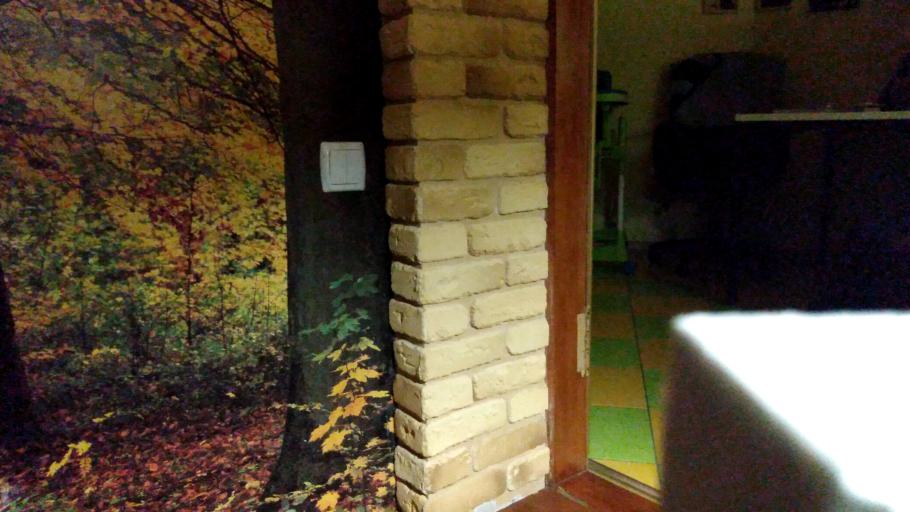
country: RU
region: Vologda
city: Lipin Bor
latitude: 60.7633
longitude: 38.0464
